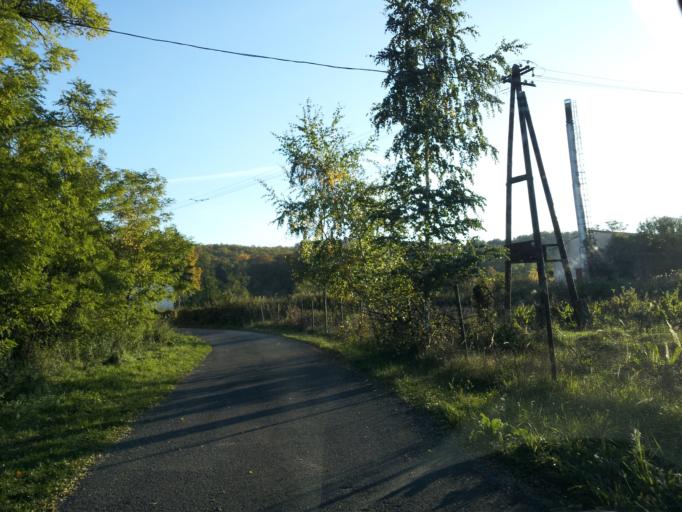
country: HU
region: Gyor-Moson-Sopron
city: Bakonyszentlaszlo
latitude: 47.3615
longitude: 17.8223
